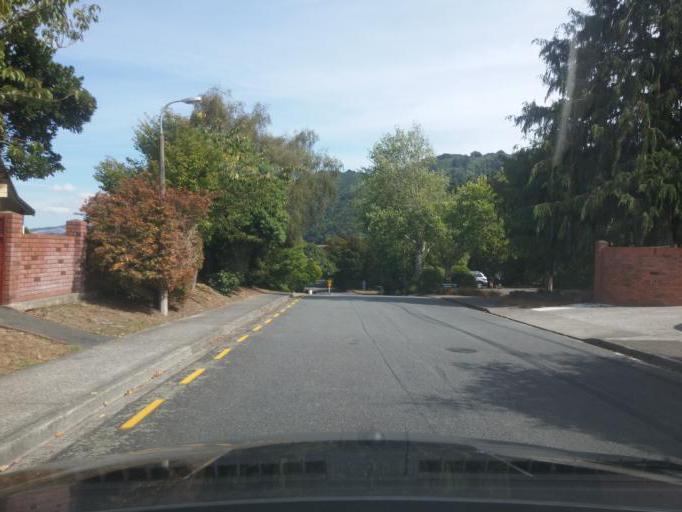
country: NZ
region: Wellington
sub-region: Upper Hutt City
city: Upper Hutt
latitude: -41.1040
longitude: 175.0953
